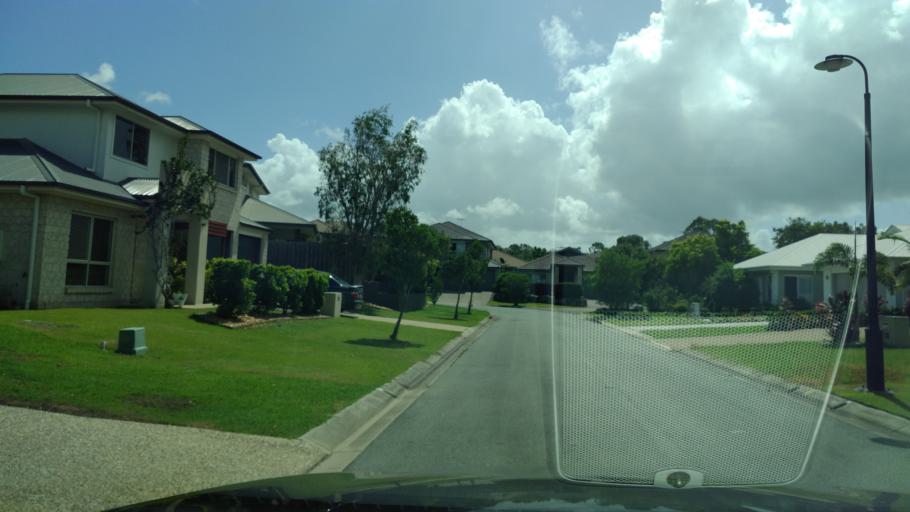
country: AU
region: Queensland
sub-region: Moreton Bay
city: Deception Bay
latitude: -27.2132
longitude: 153.0299
